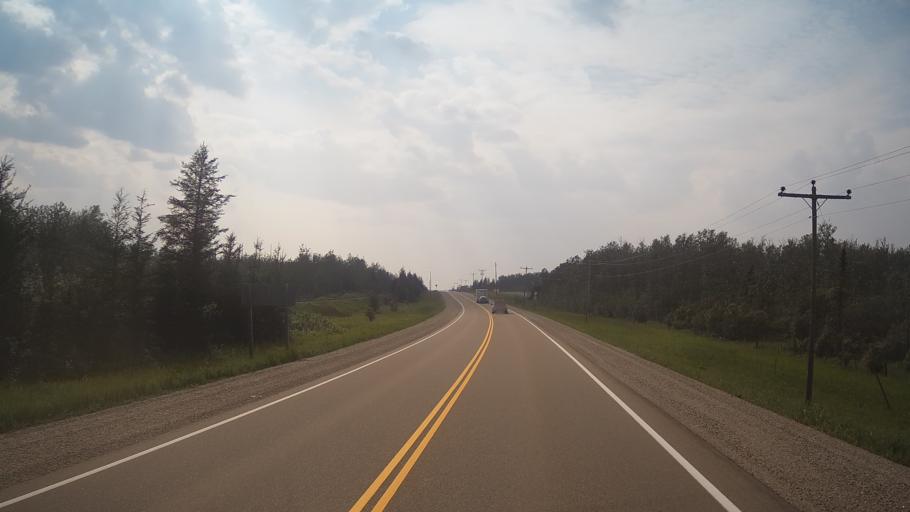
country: CA
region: Ontario
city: Kapuskasing
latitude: 49.5189
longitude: -82.8057
